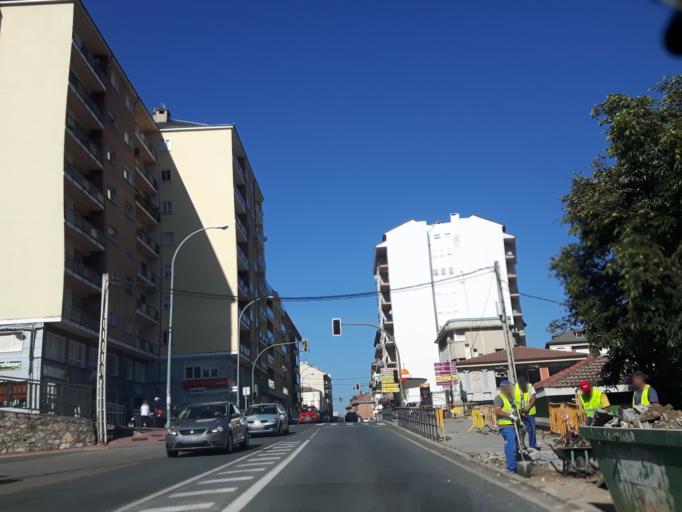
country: ES
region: Castille and Leon
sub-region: Provincia de Salamanca
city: Bejar
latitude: 40.3843
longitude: -5.7616
